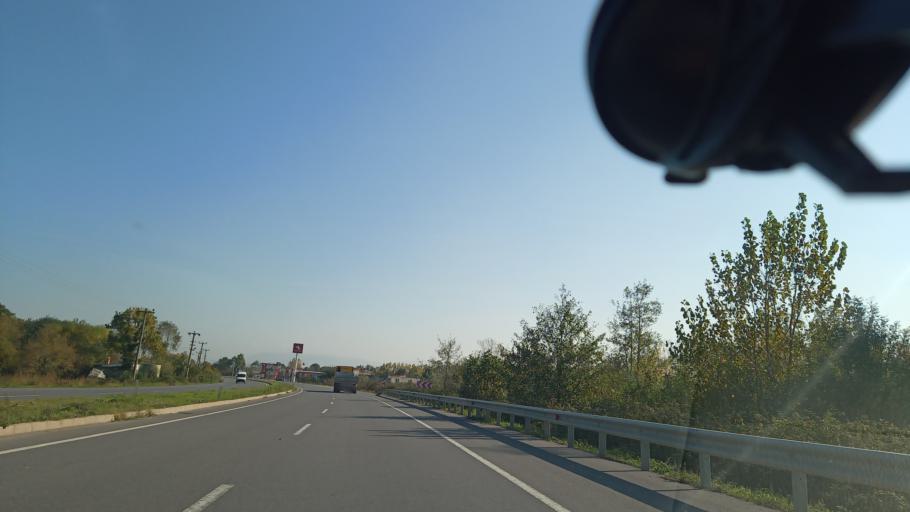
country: TR
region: Sakarya
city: Karasu
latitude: 41.0703
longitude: 30.7956
